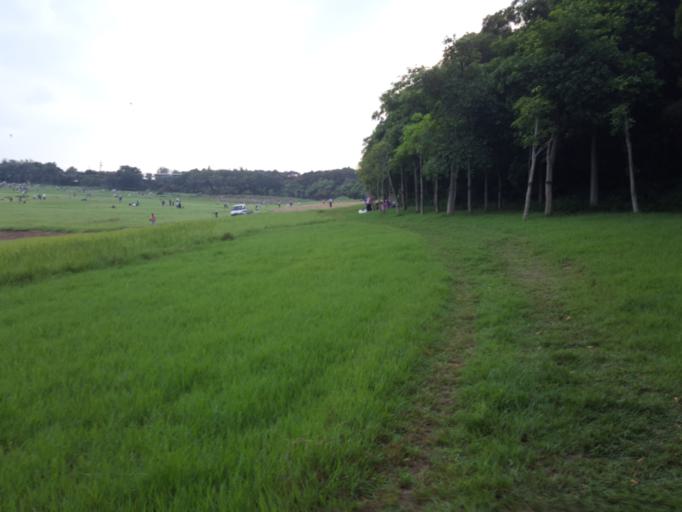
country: TW
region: Taiwan
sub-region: Hsinchu
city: Hsinchu
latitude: 24.7752
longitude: 120.9283
